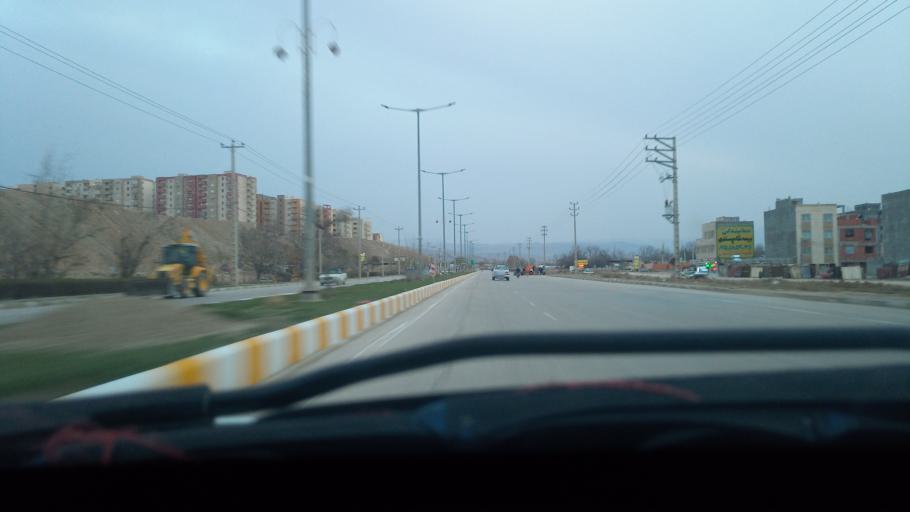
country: IR
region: Khorasan-e Shomali
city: Bojnurd
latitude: 37.4529
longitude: 57.3176
